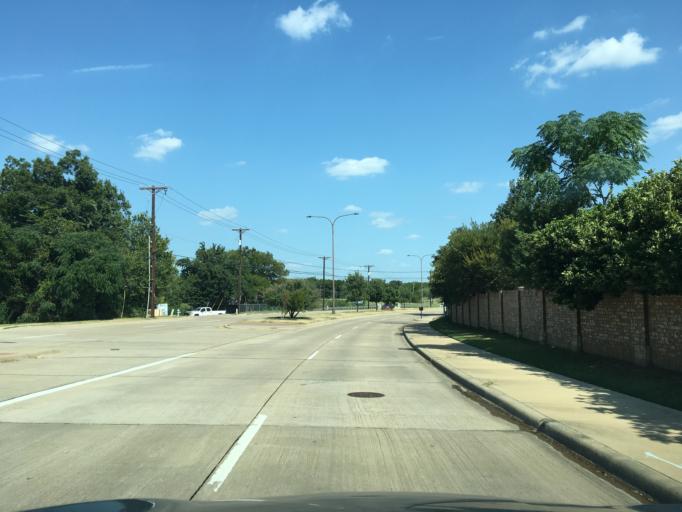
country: US
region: Texas
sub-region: Tarrant County
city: Dalworthington Gardens
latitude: 32.6801
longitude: -97.1599
